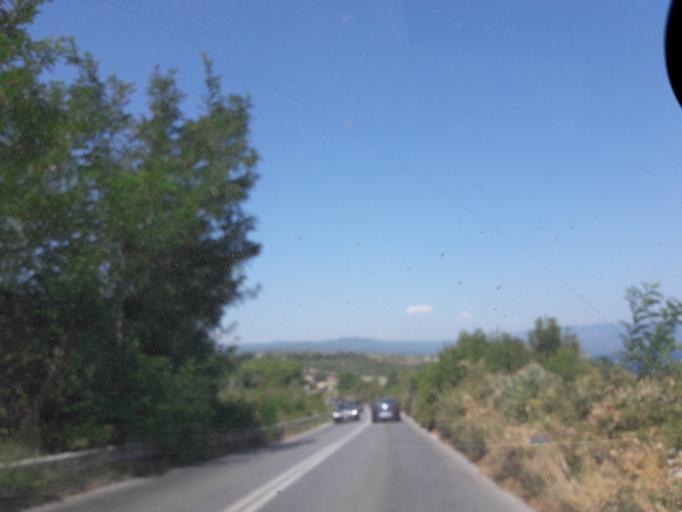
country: GR
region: Central Macedonia
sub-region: Nomos Chalkidikis
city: Ierissos
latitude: 40.3854
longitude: 23.8972
